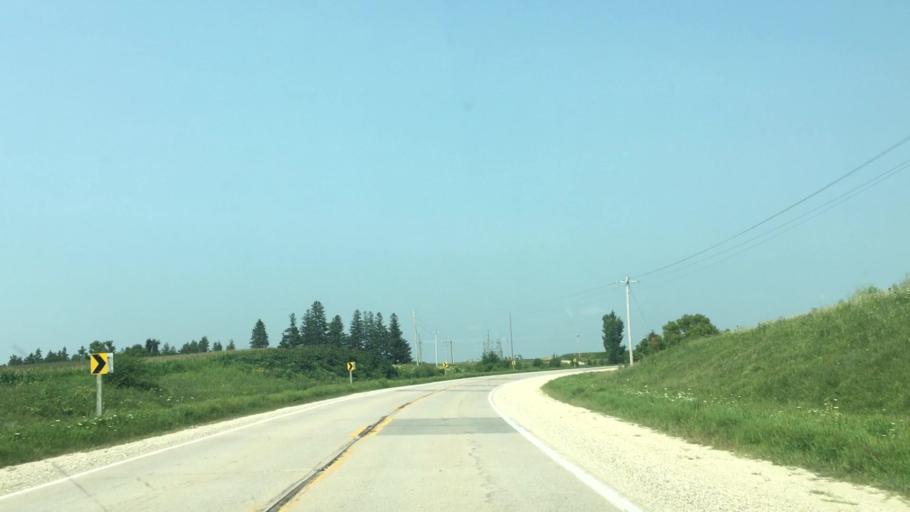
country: US
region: Iowa
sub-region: Fayette County
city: West Union
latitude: 43.1369
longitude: -91.8691
